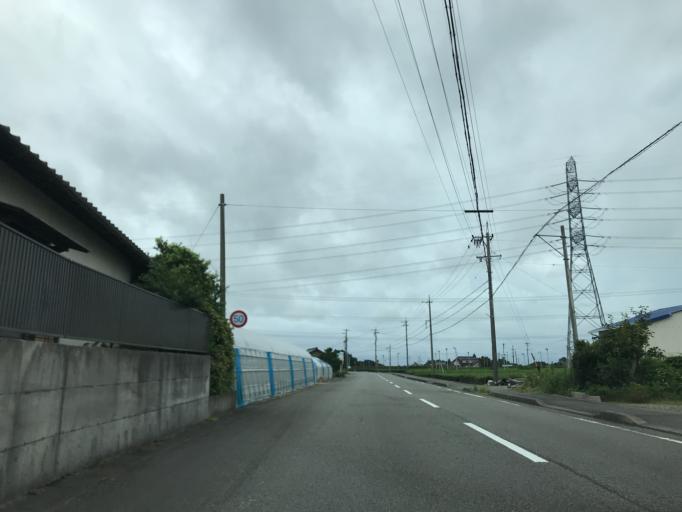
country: JP
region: Shizuoka
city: Sagara
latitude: 34.6955
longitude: 138.1436
